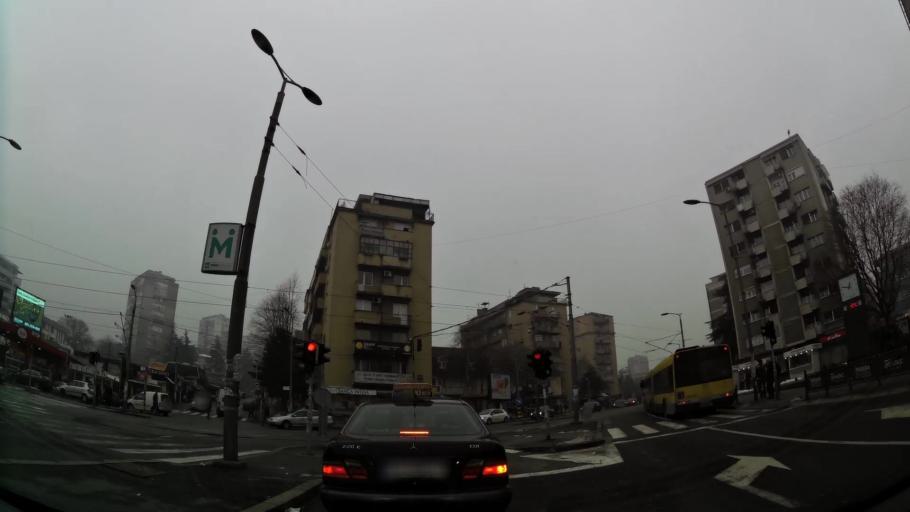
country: RS
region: Central Serbia
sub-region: Belgrade
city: Cukarica
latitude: 44.7822
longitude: 20.4180
